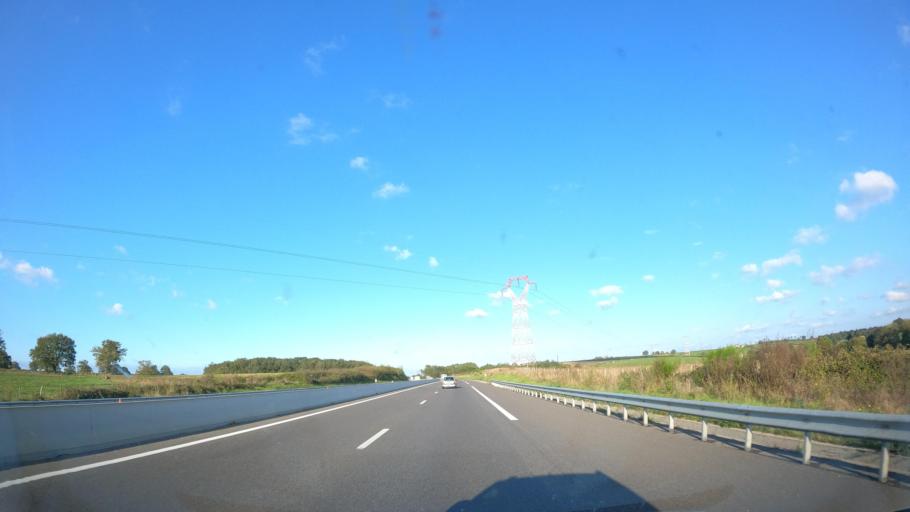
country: FR
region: Bourgogne
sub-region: Departement de Saone-et-Loire
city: Saint-Eusebe
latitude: 46.7137
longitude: 4.4335
